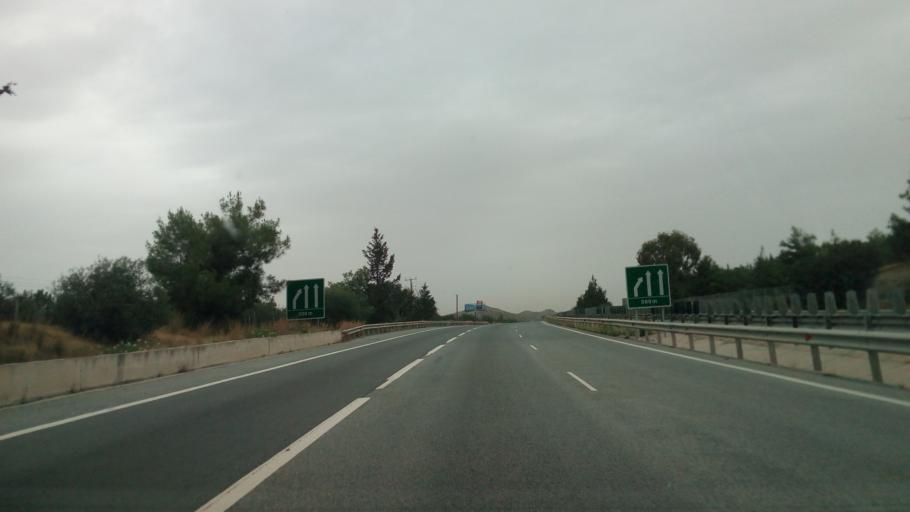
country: CY
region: Larnaka
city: Kofinou
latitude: 34.8591
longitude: 33.3941
